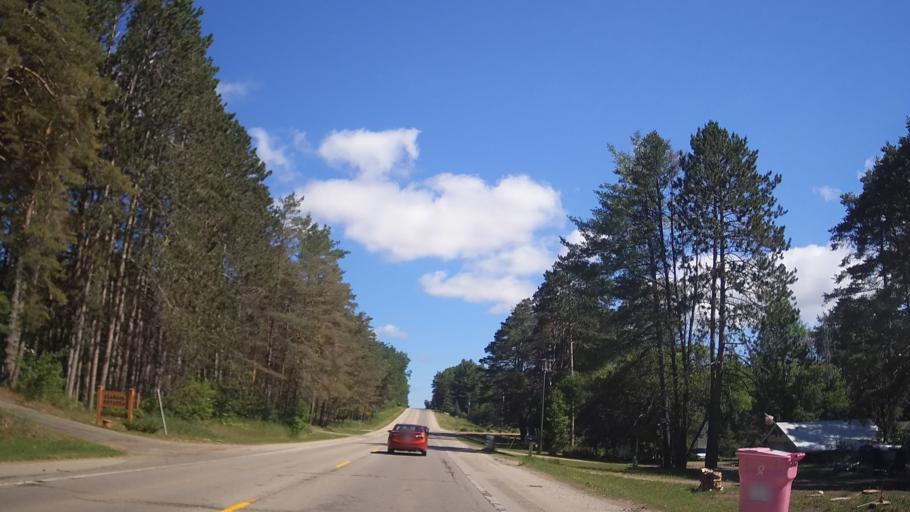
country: US
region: Michigan
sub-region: Cheboygan County
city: Indian River
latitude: 45.4542
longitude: -84.7840
